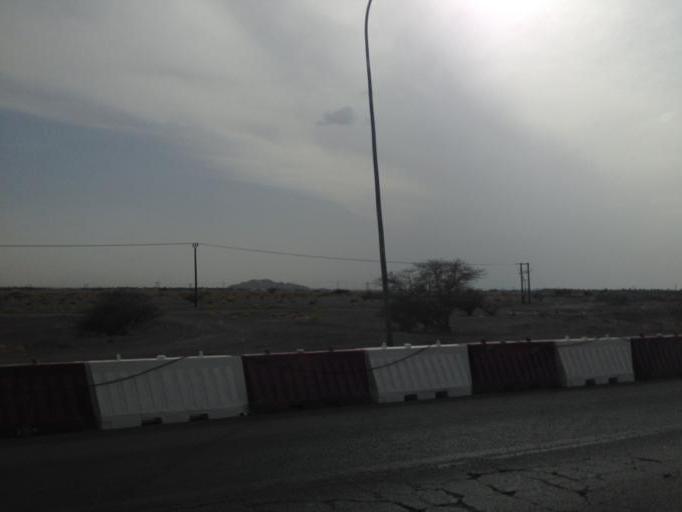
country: OM
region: Ash Sharqiyah
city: Al Qabil
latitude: 22.5576
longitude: 58.7130
